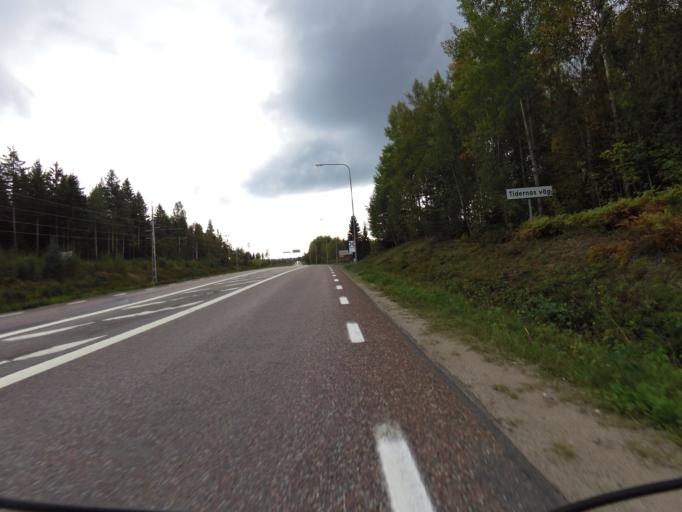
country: SE
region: Gaevleborg
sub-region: Ockelbo Kommun
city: Ockelbo
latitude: 60.8740
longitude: 16.7048
